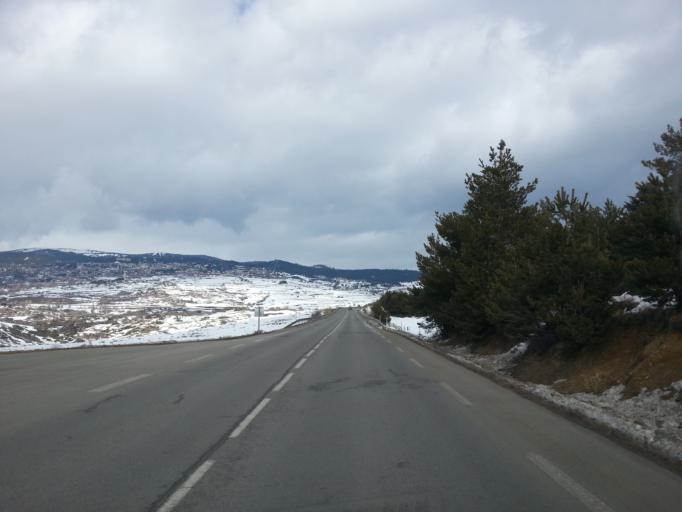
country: ES
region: Catalonia
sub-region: Provincia de Girona
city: Llivia
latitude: 42.4729
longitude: 2.0547
